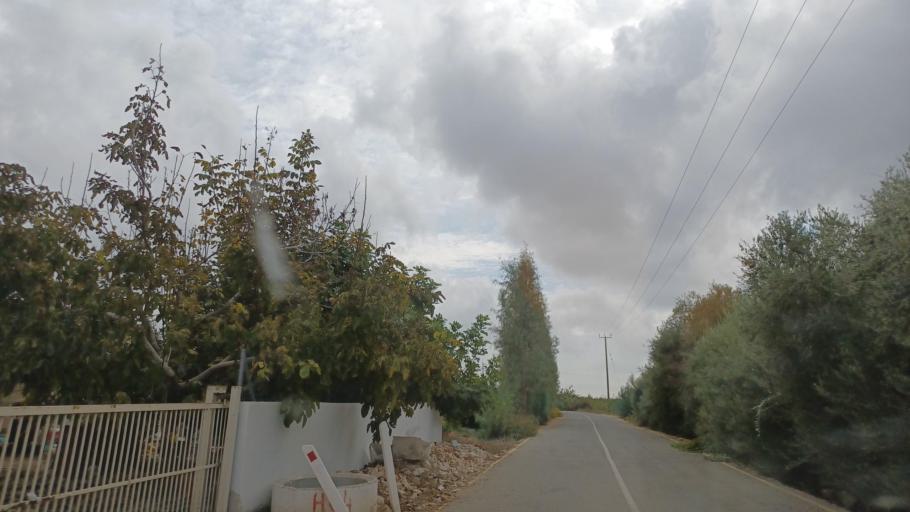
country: CY
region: Pafos
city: Kissonerga
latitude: 34.8304
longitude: 32.4142
